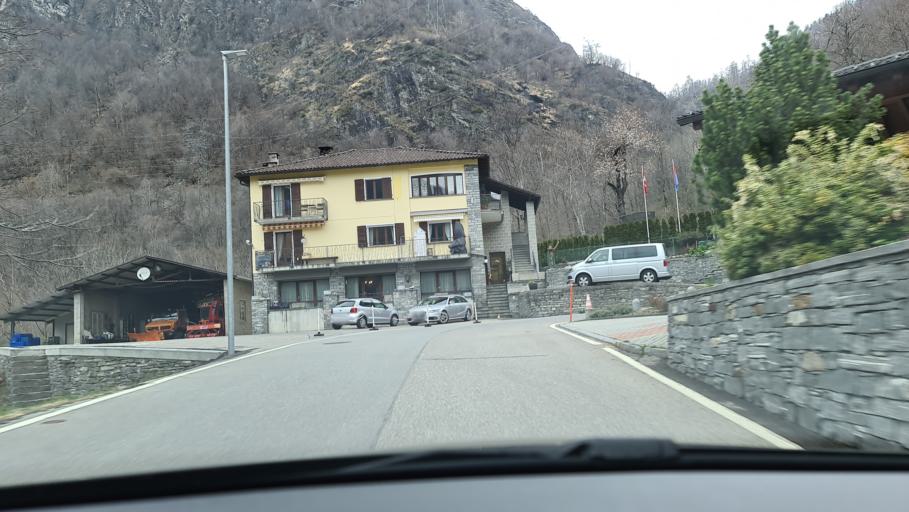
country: CH
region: Ticino
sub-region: Vallemaggia District
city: Cevio
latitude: 46.4082
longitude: 8.6479
